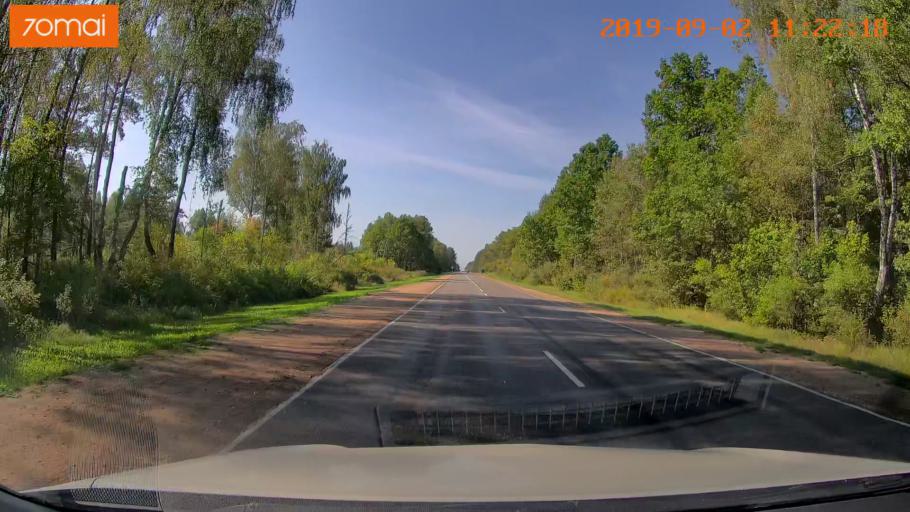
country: RU
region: Smolensk
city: Roslavl'
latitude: 54.0273
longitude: 33.0169
